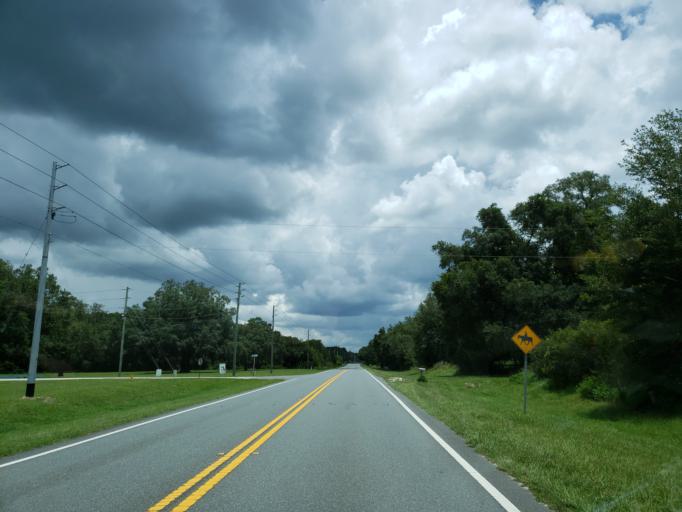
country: US
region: Florida
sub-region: Sumter County
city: Bushnell
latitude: 28.6198
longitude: -82.2035
